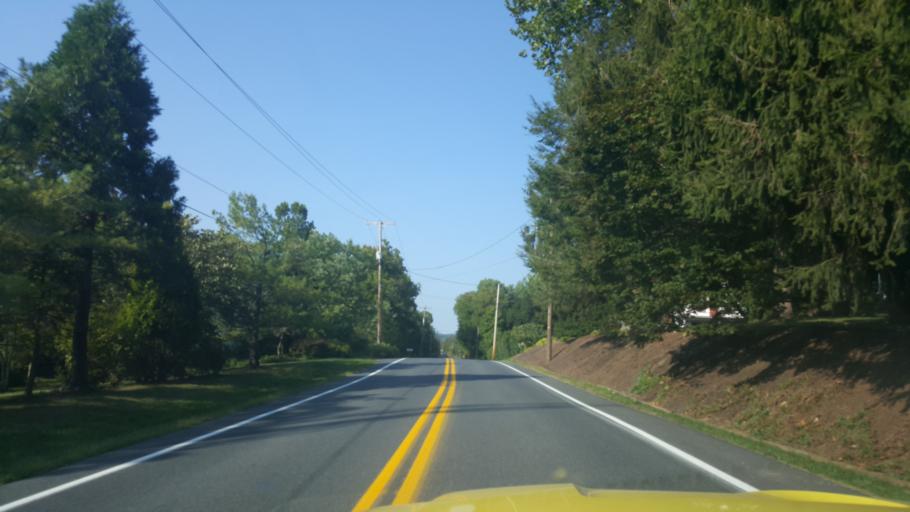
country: US
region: Pennsylvania
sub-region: Lebanon County
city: Campbelltown
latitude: 40.2225
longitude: -76.5374
